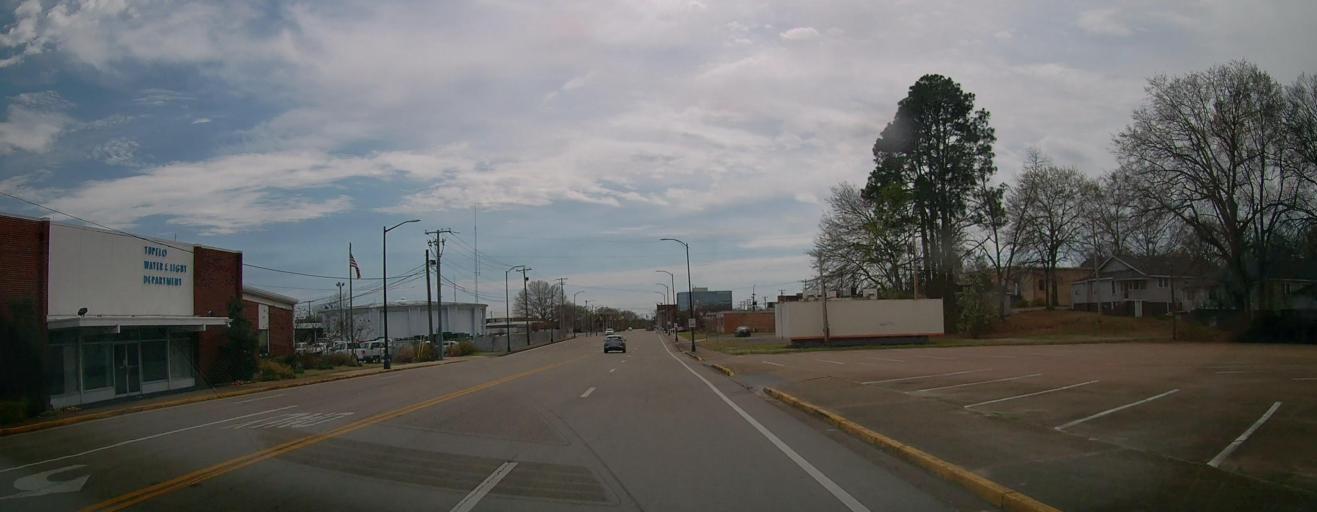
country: US
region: Mississippi
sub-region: Lee County
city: Tupelo
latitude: 34.2618
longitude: -88.7035
